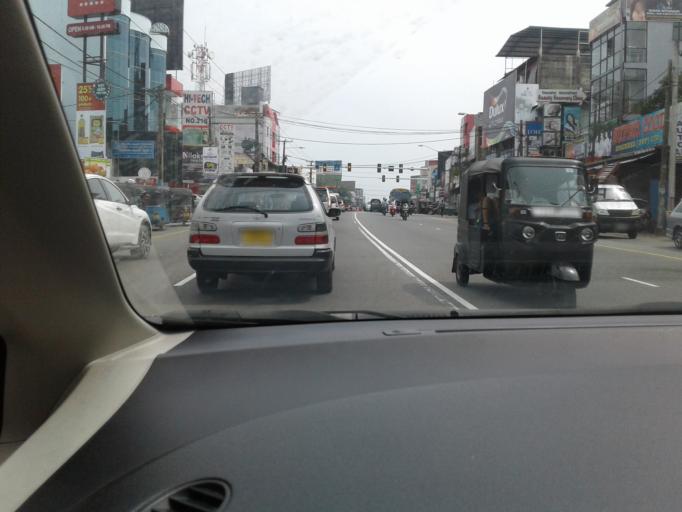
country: LK
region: Western
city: Maharagama
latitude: 6.8516
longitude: 79.9204
